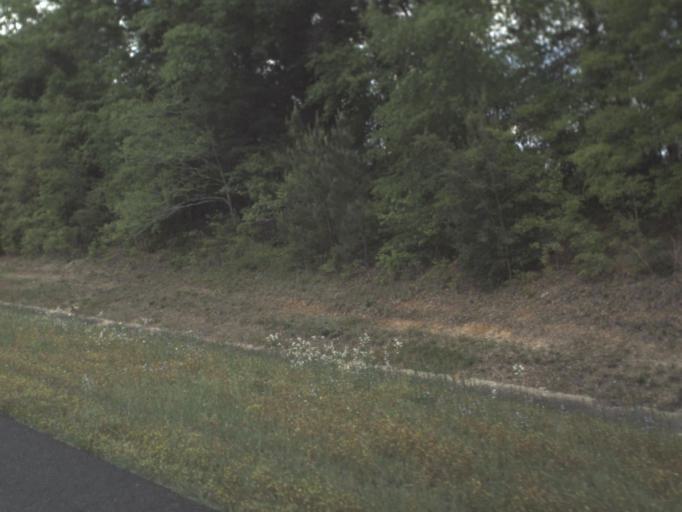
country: US
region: Florida
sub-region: Escambia County
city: Molino
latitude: 30.8530
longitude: -87.3226
